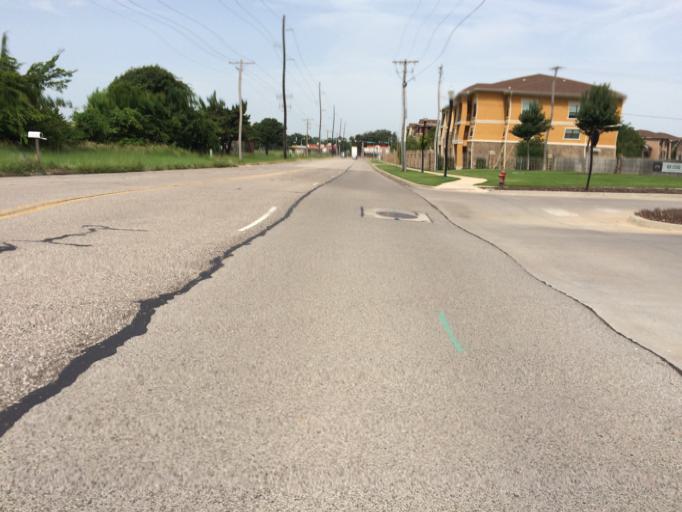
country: US
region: Oklahoma
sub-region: Cleveland County
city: Norman
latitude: 35.1897
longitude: -97.4182
